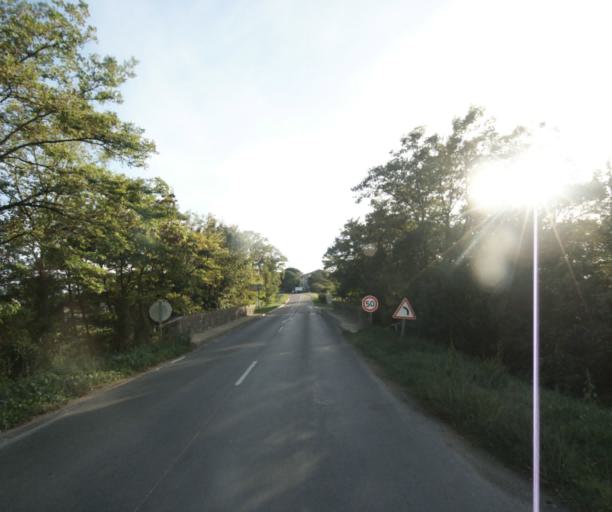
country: FR
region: Midi-Pyrenees
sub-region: Departement du Gers
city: Gondrin
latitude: 43.8895
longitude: 0.2403
